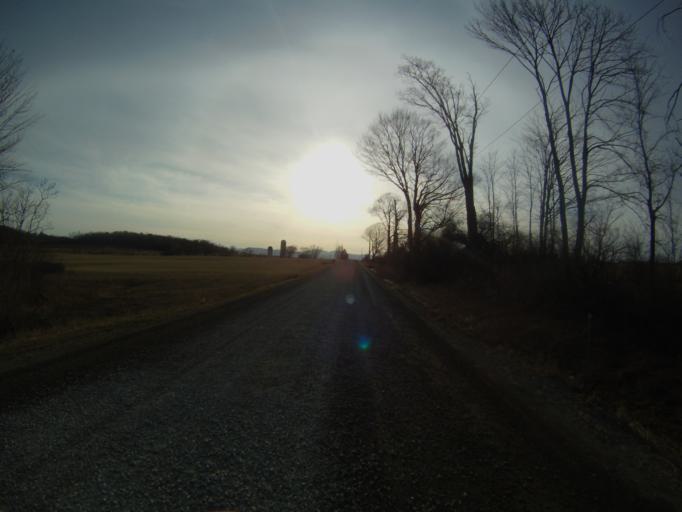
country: US
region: Vermont
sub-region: Addison County
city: Middlebury (village)
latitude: 44.0403
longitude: -73.2829
